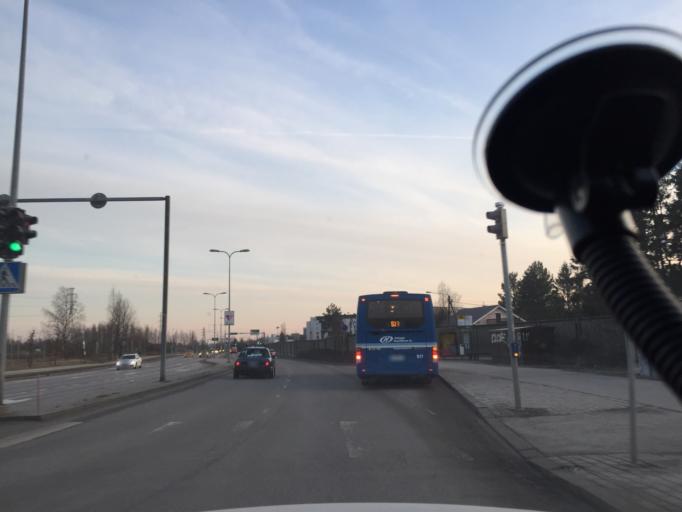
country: FI
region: Uusimaa
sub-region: Helsinki
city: Vantaa
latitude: 60.2724
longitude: 24.9694
